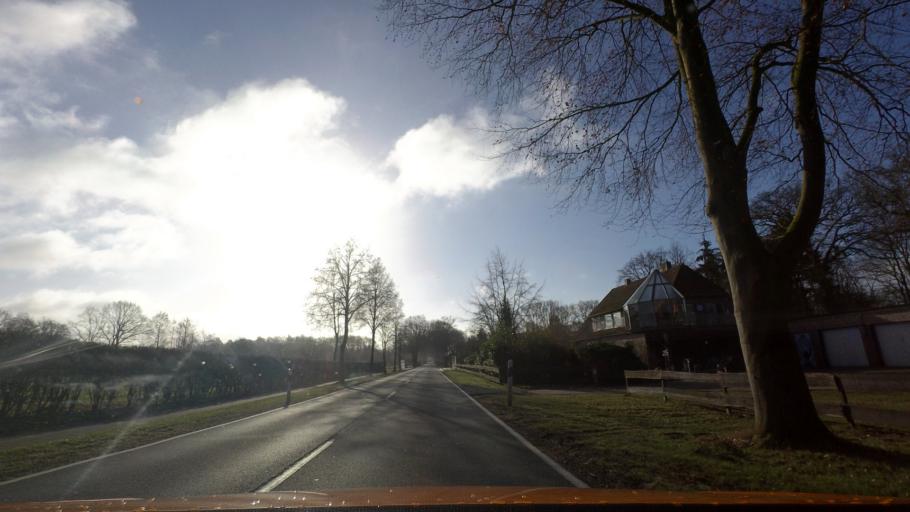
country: DE
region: Lower Saxony
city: Wardenburg
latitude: 53.0183
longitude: 8.2454
